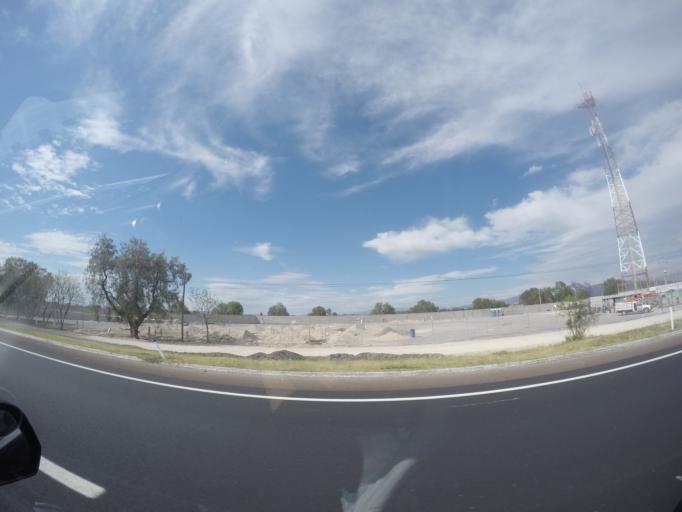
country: MX
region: Guanajuato
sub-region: Celaya
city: La Trinidad
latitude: 20.5524
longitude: -100.7684
